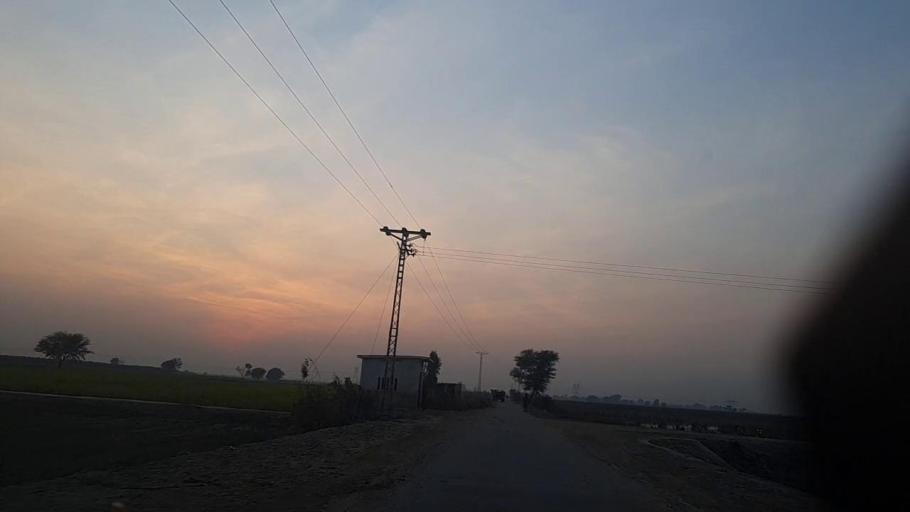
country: PK
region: Sindh
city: Sakrand
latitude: 26.0992
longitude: 68.3356
